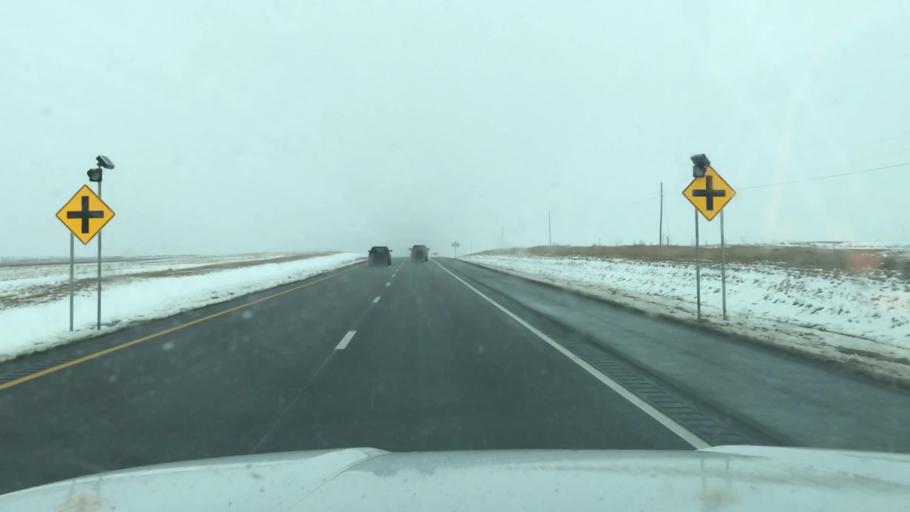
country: US
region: Missouri
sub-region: DeKalb County
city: Maysville
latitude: 39.7615
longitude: -94.3690
